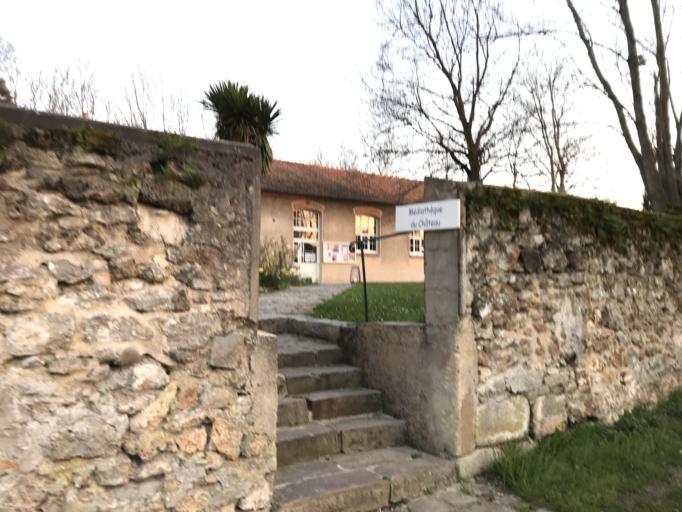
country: FR
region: Ile-de-France
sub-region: Departement de l'Essonne
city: Ballainvilliers
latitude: 48.6721
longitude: 2.2932
